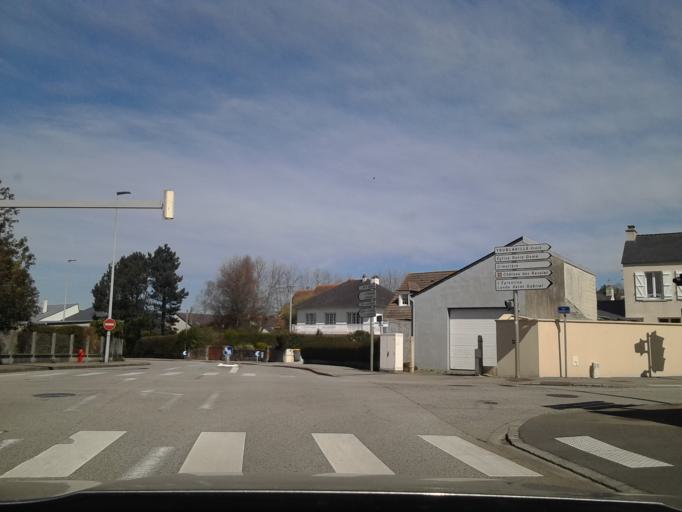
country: FR
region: Lower Normandy
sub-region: Departement de la Manche
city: Tourlaville
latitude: 49.6400
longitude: -1.5729
